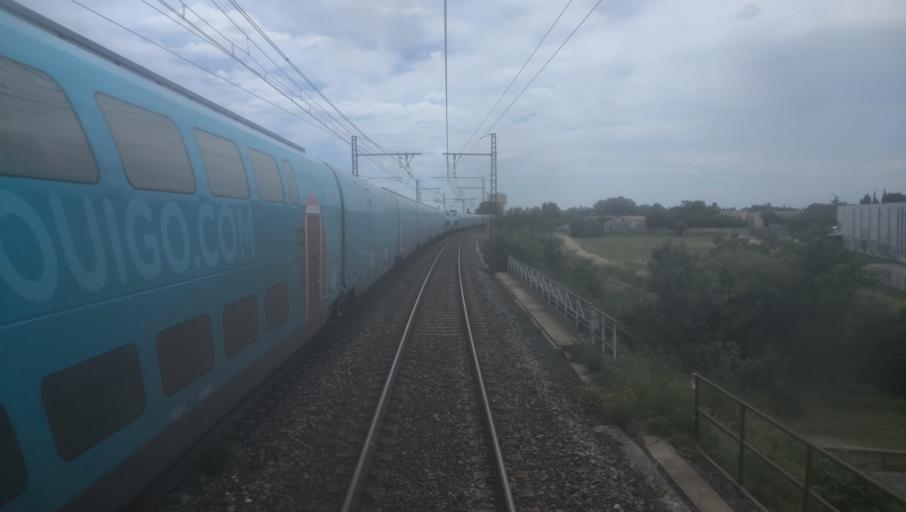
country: FR
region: Languedoc-Roussillon
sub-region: Departement de l'Herault
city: Lunel
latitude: 43.6868
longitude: 4.1462
